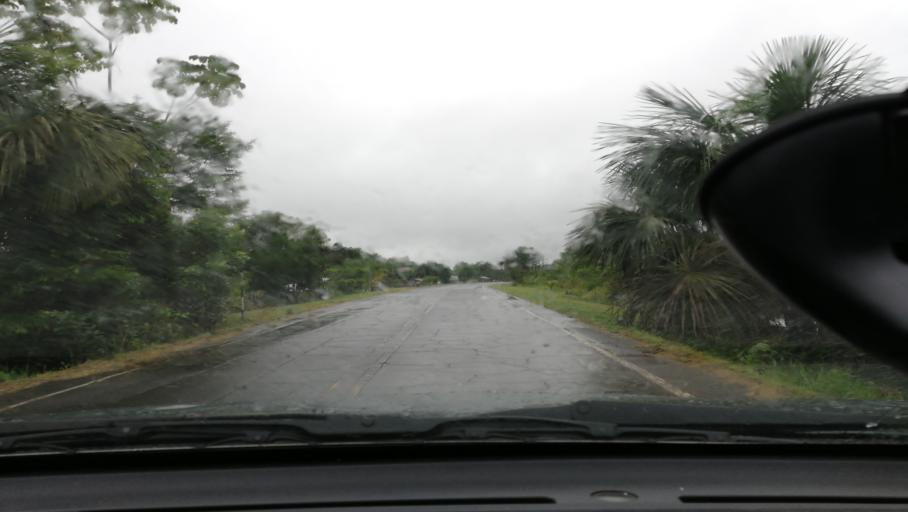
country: PE
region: Loreto
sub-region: Provincia de Maynas
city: San Juan
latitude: -4.0987
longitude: -73.4549
